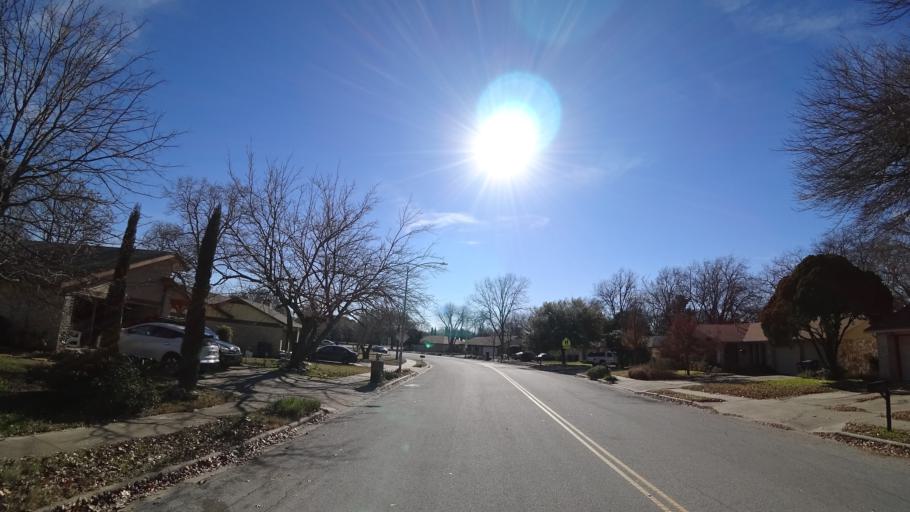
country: US
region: Texas
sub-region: Travis County
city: Wells Branch
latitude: 30.3803
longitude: -97.7044
